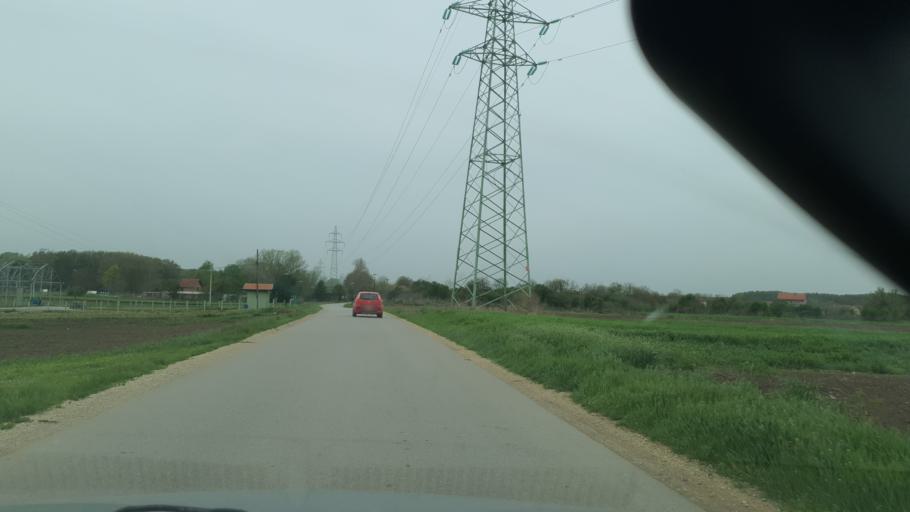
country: RS
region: Central Serbia
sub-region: Branicevski Okrug
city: Pozarevac
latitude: 44.7120
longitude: 21.1248
